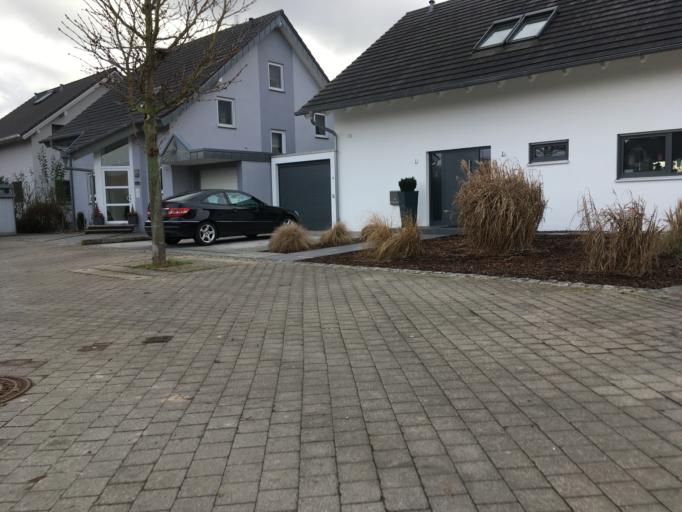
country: DE
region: Baden-Wuerttemberg
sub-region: Regierungsbezirk Stuttgart
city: Nordheim
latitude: 49.1133
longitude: 9.1668
